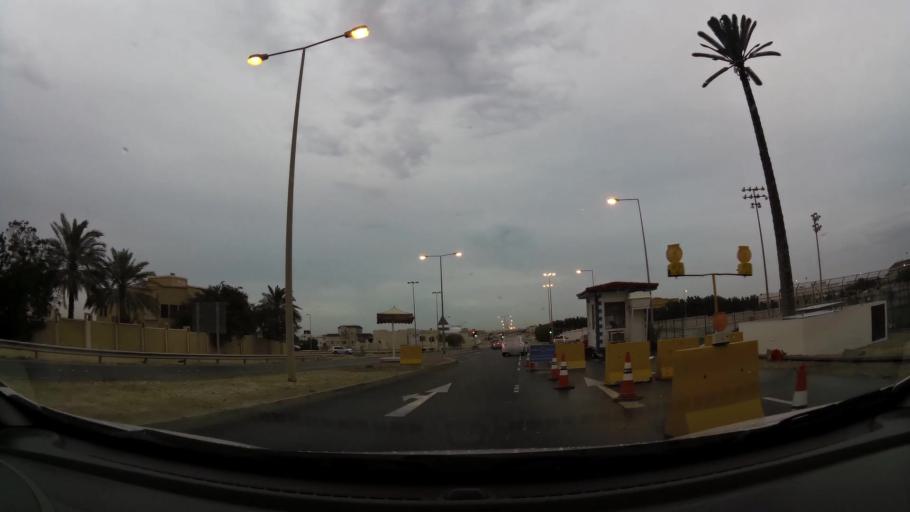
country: BH
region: Central Governorate
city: Madinat Hamad
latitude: 26.1403
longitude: 50.5171
